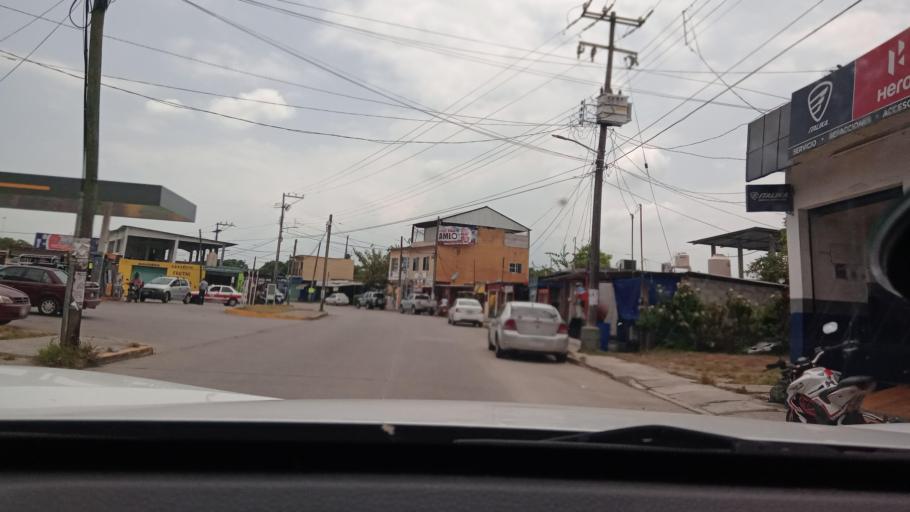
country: MX
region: Veracruz
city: Las Choapas
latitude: 17.8999
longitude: -94.0989
